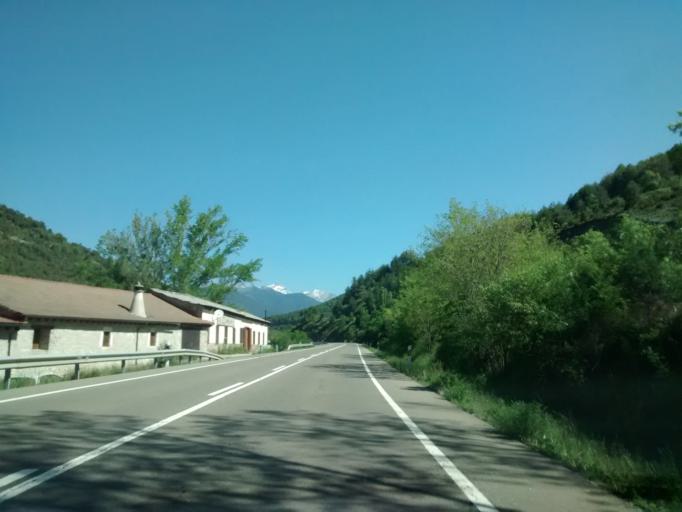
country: ES
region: Aragon
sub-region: Provincia de Huesca
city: Jaca
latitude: 42.5984
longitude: -0.5438
